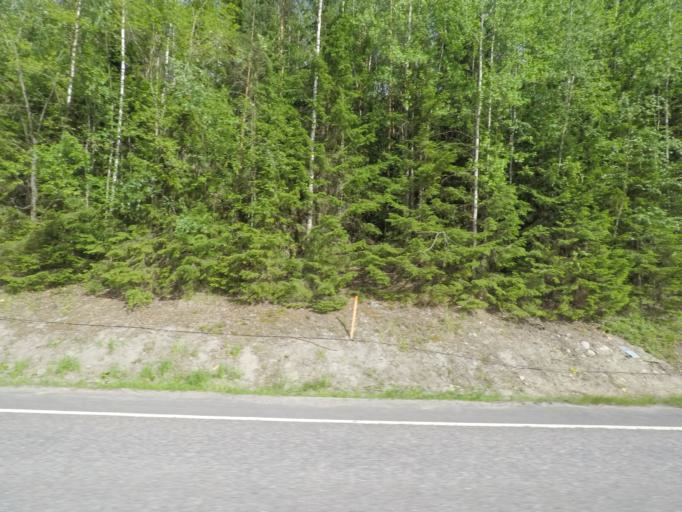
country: FI
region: Uusimaa
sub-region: Porvoo
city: Pukkila
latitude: 60.7961
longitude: 25.4690
